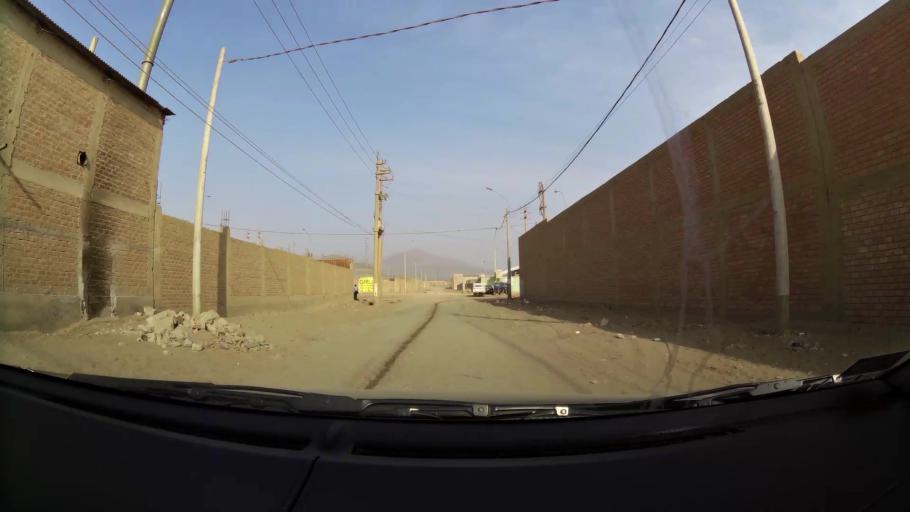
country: PE
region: Lima
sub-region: Lima
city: Santa Rosa
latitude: -11.7571
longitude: -77.1567
